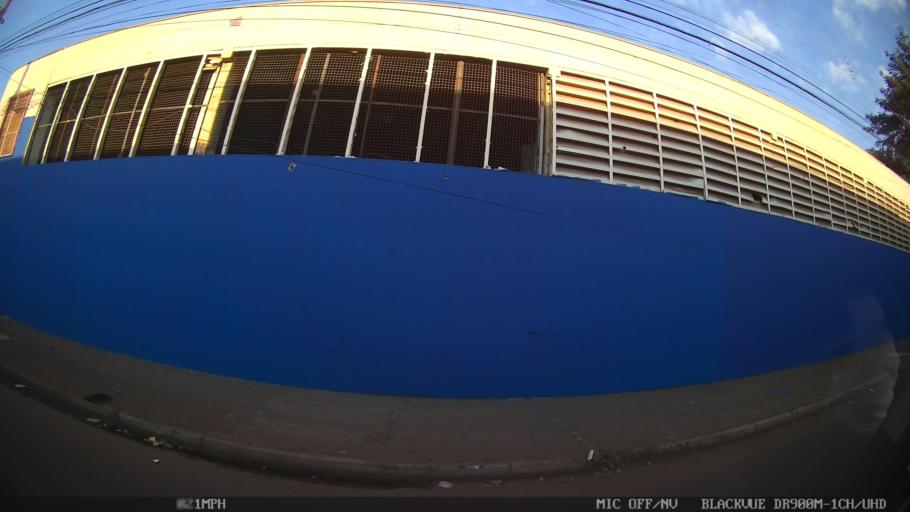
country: BR
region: Sao Paulo
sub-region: Ribeirao Preto
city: Ribeirao Preto
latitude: -21.1409
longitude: -47.7892
